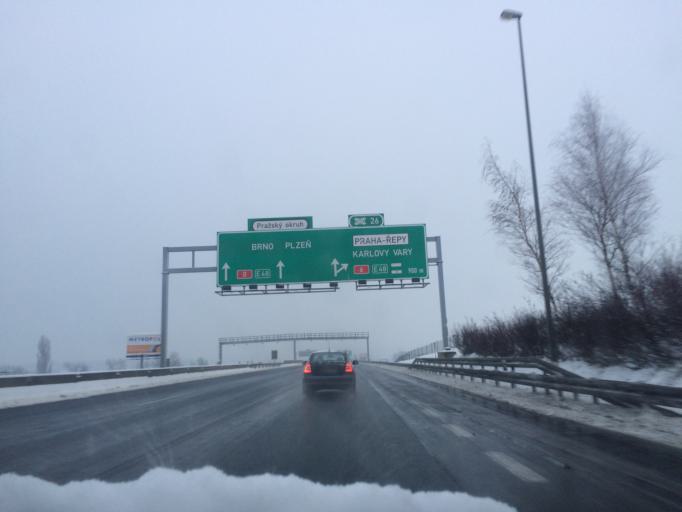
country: CZ
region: Central Bohemia
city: Hostivice
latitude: 50.0889
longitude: 14.2952
